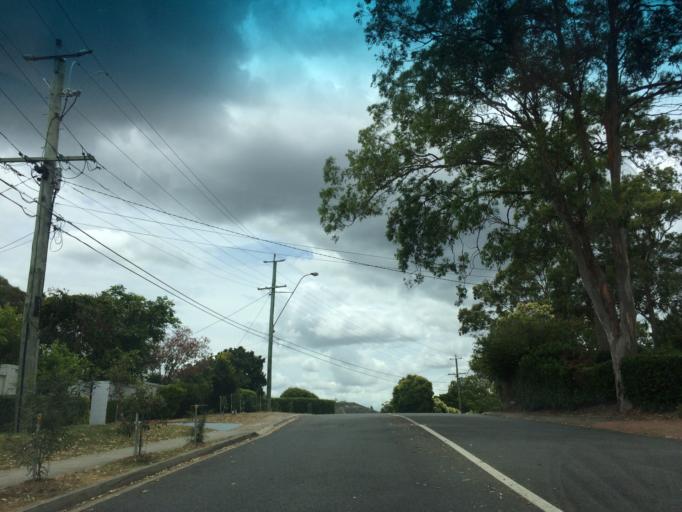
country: AU
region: Queensland
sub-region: Brisbane
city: Kenmore Hills
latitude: -27.5197
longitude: 152.9417
